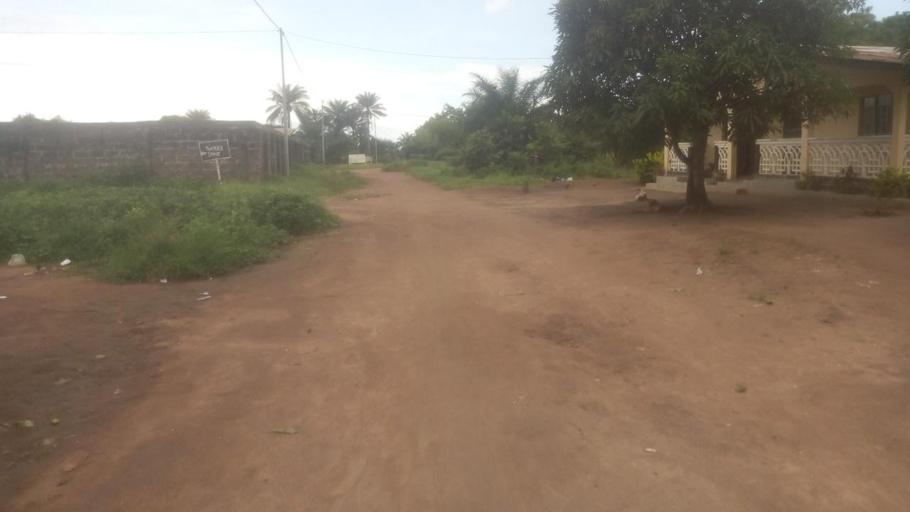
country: SL
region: Northern Province
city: Masoyila
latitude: 8.5872
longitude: -13.1663
